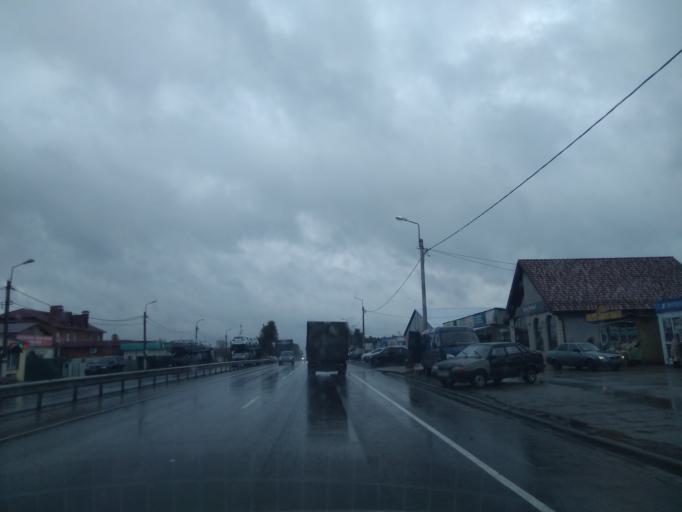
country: RU
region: Tula
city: Teploye
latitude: 53.6209
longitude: 37.5922
